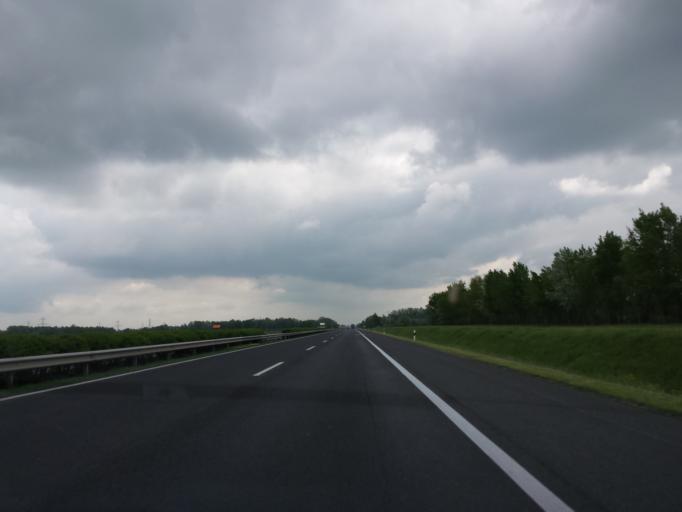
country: HU
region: Gyor-Moson-Sopron
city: Mosonszentmiklos
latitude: 47.7246
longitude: 17.4557
